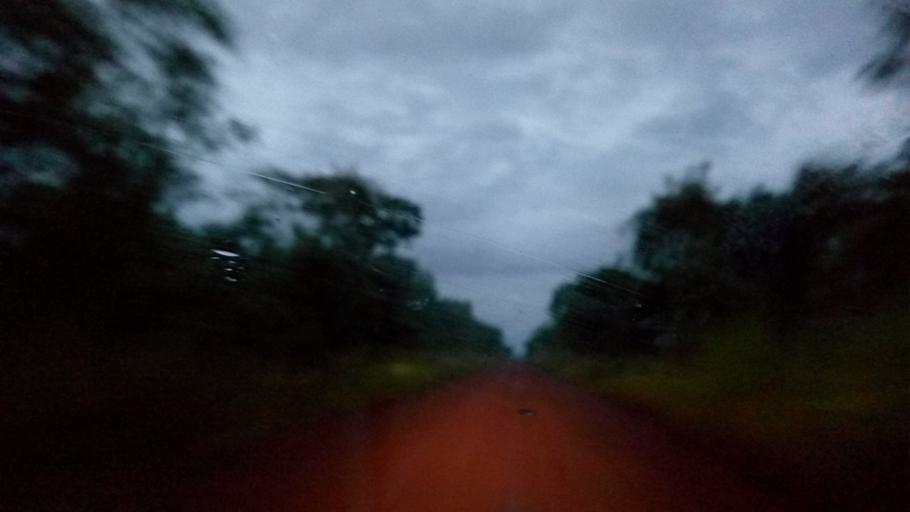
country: ZM
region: Luapula
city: Nchelenge
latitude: -9.7883
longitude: 28.1602
